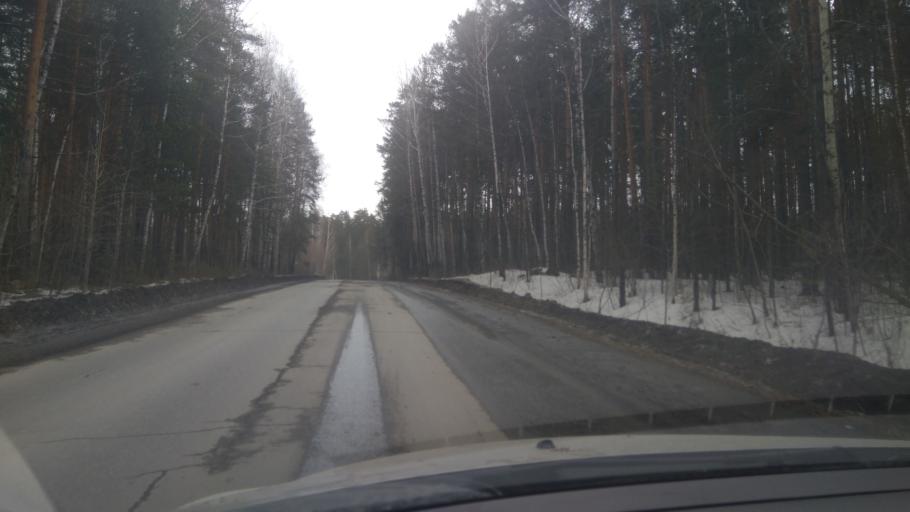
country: RU
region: Sverdlovsk
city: Severka
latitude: 56.8347
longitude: 60.3831
